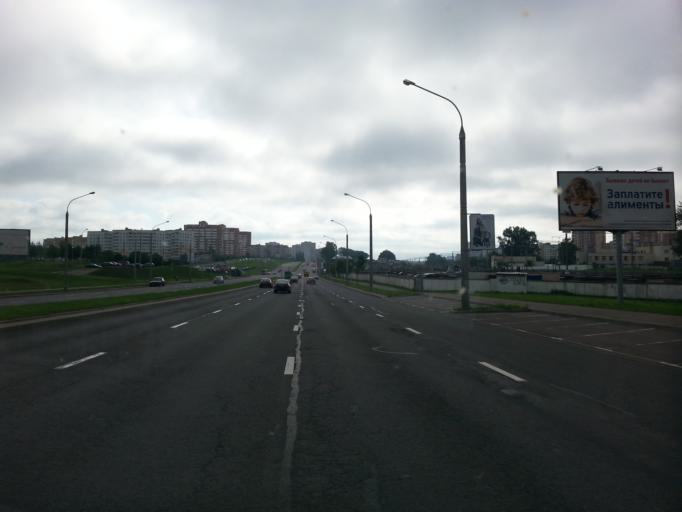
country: BY
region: Minsk
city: Novoye Medvezhino
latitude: 53.9300
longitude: 27.4844
